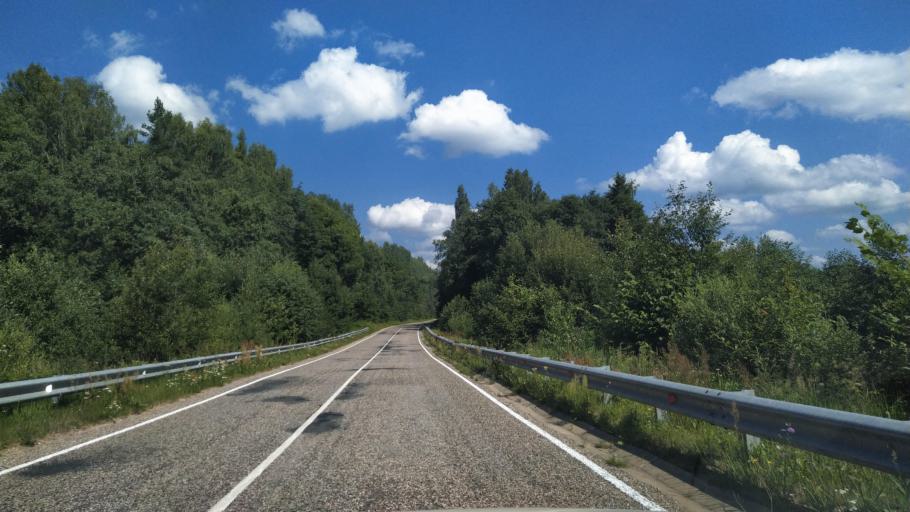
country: RU
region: Pskov
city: Pushkinskiye Gory
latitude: 57.0633
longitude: 28.9493
